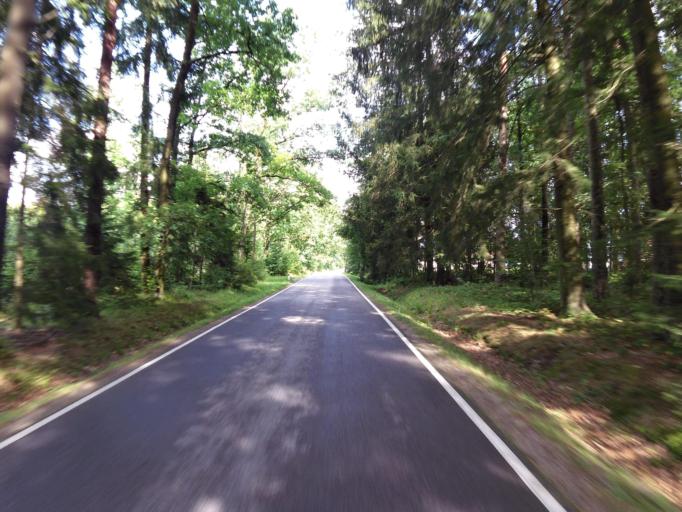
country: CZ
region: Jihocesky
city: Suchdol nad Luznici
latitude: 48.8885
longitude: 14.8369
